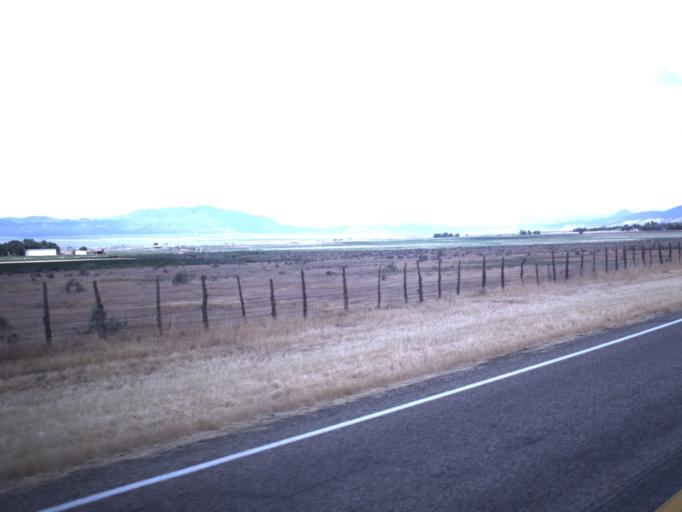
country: US
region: Utah
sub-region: Iron County
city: Parowan
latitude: 37.8700
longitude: -112.7956
